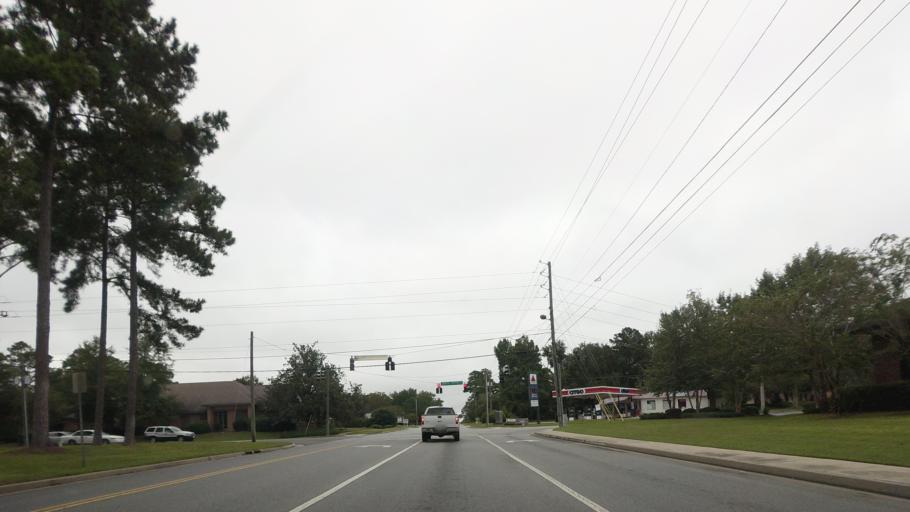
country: US
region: Georgia
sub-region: Lowndes County
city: Remerton
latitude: 30.8685
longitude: -83.2921
